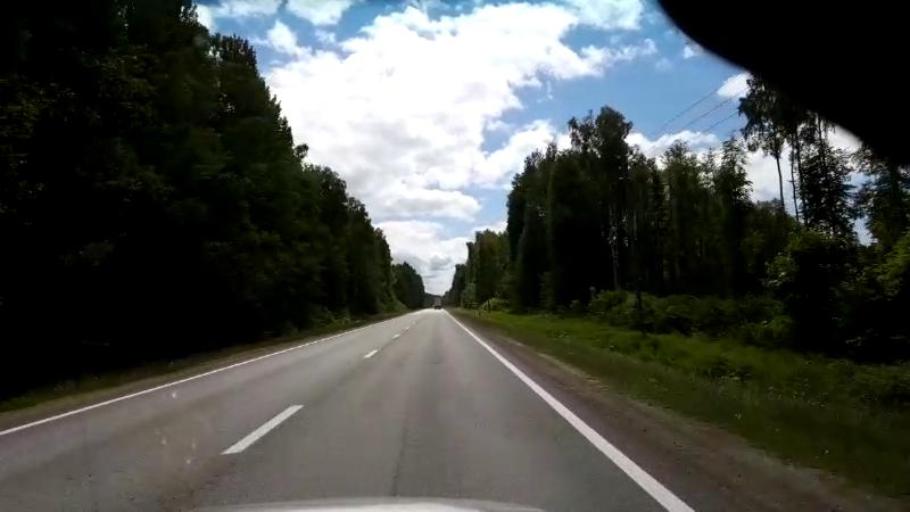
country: LV
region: Salacgrivas
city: Salacgriva
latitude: 57.5858
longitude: 24.4241
